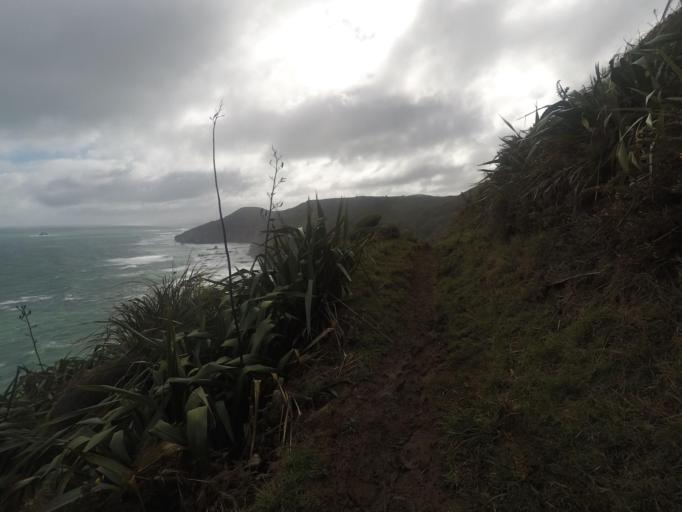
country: NZ
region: Auckland
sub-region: Auckland
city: Muriwai Beach
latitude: -36.8715
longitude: 174.4335
